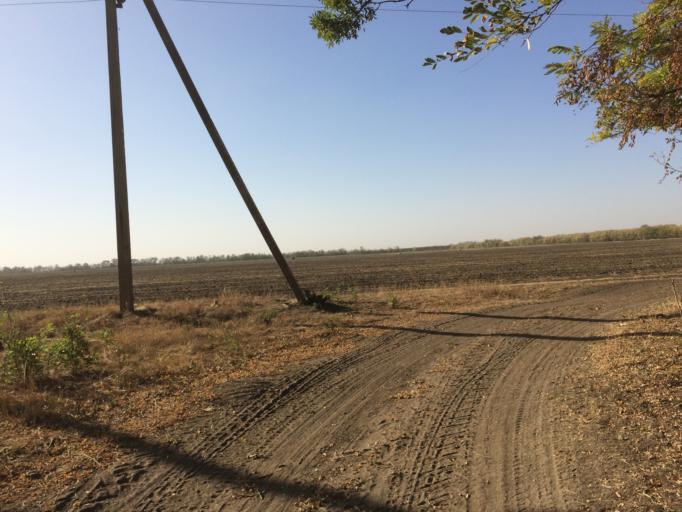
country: RU
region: Rostov
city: Tselina
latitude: 46.5247
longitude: 41.1810
